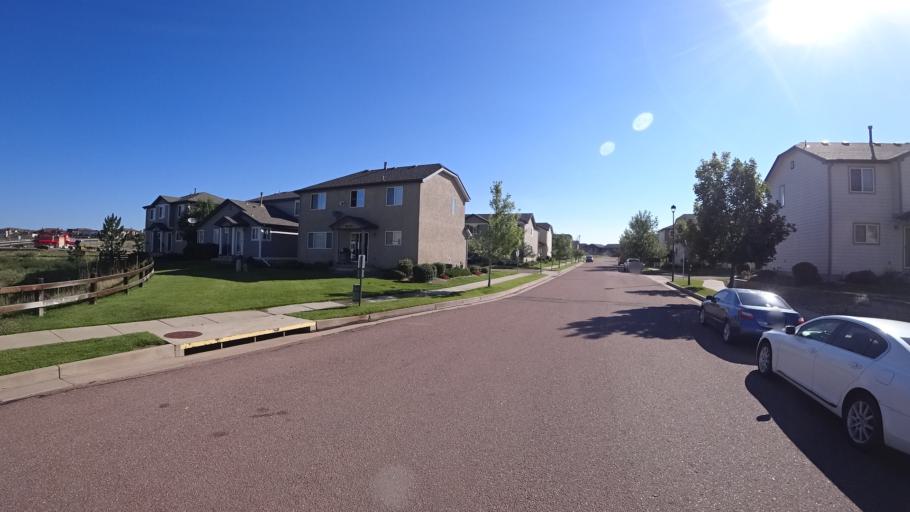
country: US
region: Colorado
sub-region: El Paso County
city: Gleneagle
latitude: 38.9980
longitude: -104.7964
